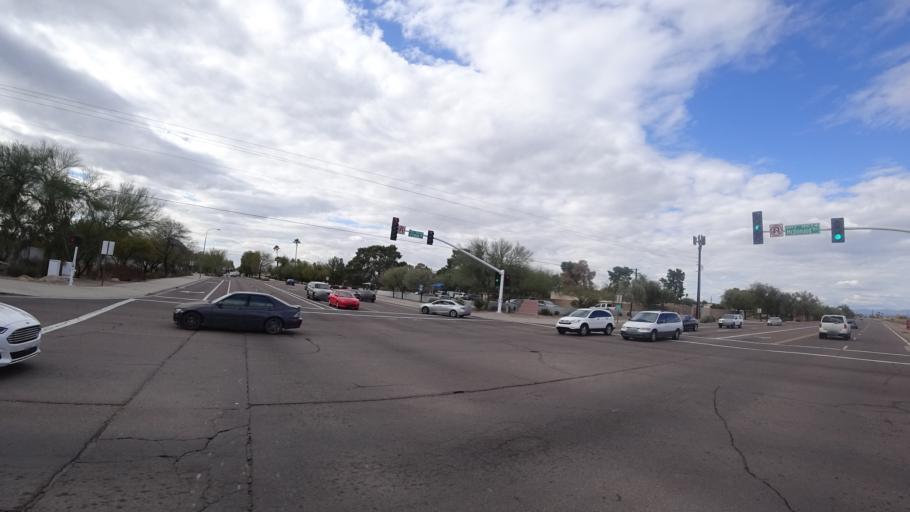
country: US
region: Arizona
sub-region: Maricopa County
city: Scottsdale
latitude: 33.5237
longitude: -111.8915
